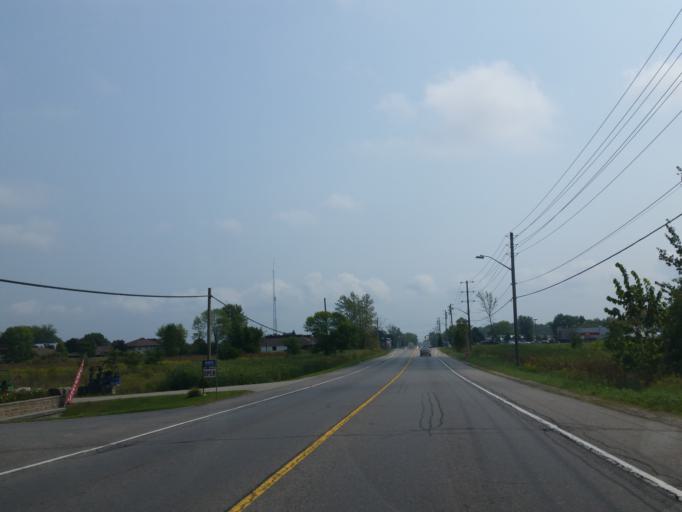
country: CA
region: Ontario
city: Brockville
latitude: 44.6056
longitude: -75.7195
